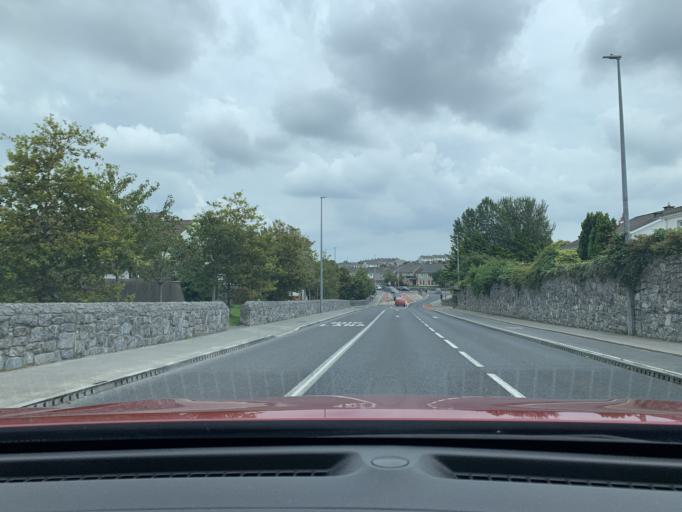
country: IE
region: Connaught
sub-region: County Galway
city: Gaillimh
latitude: 53.2740
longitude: -9.0873
